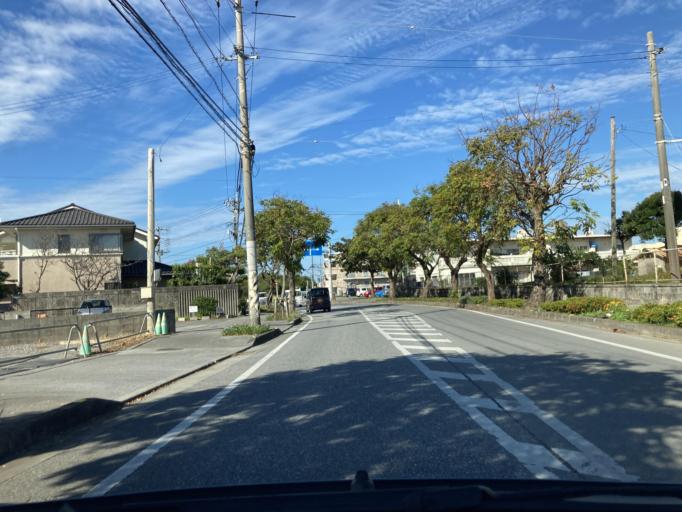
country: JP
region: Okinawa
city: Okinawa
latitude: 26.3701
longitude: 127.7480
